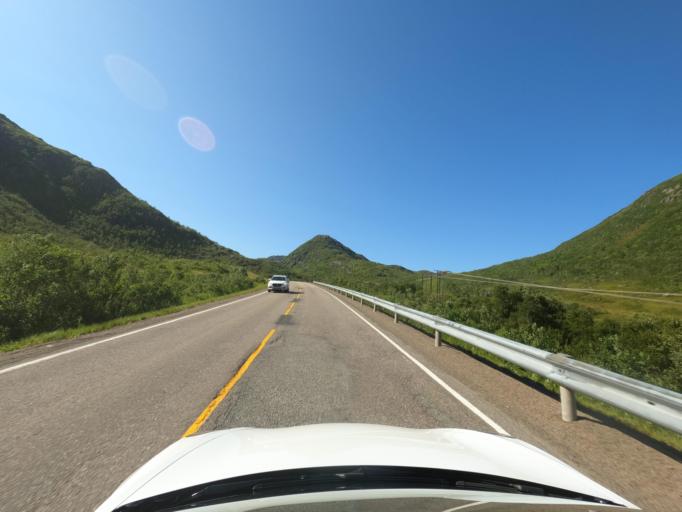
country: NO
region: Nordland
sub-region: Lodingen
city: Lodingen
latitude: 68.4909
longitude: 15.6948
